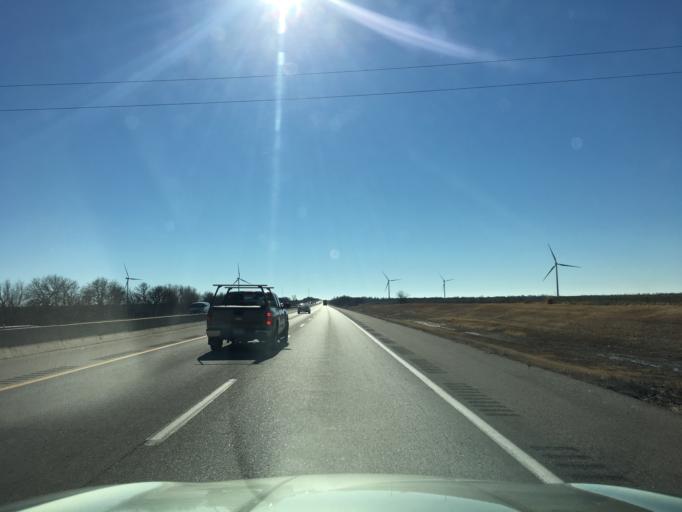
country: US
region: Kansas
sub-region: Sumner County
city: Wellington
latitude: 37.1452
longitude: -97.3395
